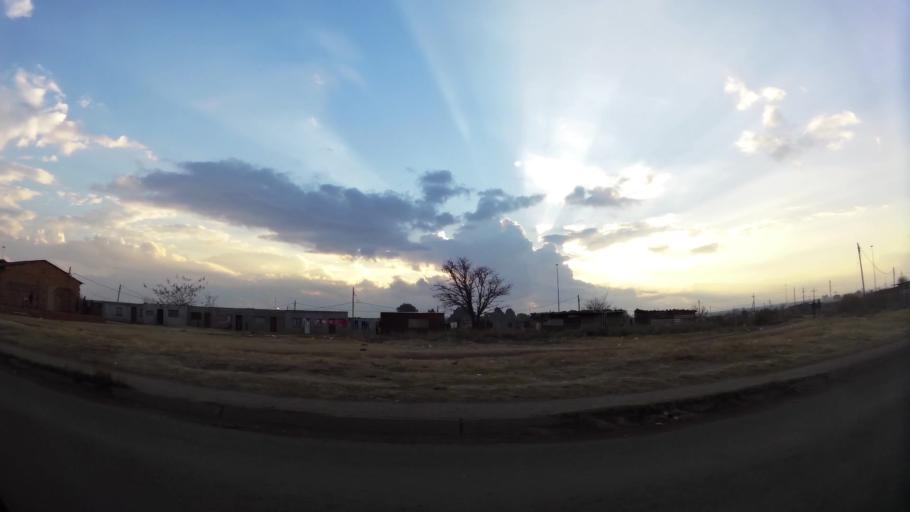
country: ZA
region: Gauteng
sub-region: City of Johannesburg Metropolitan Municipality
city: Orange Farm
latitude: -26.5518
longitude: 27.8404
